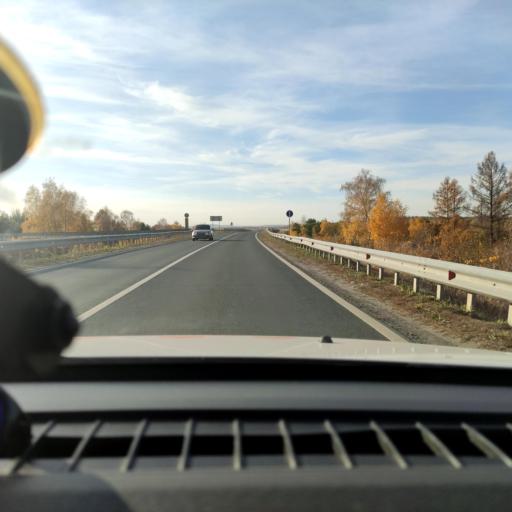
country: RU
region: Samara
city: Bereza
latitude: 53.4907
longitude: 50.1176
